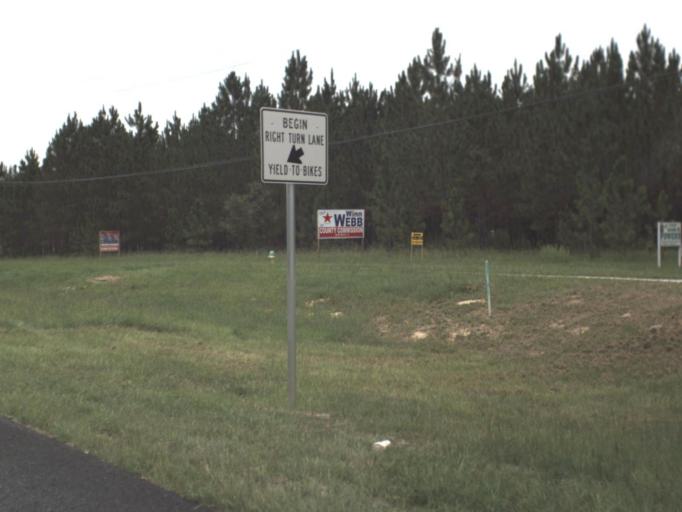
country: US
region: Florida
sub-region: Citrus County
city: Citrus Hills
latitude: 28.8573
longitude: -82.4172
